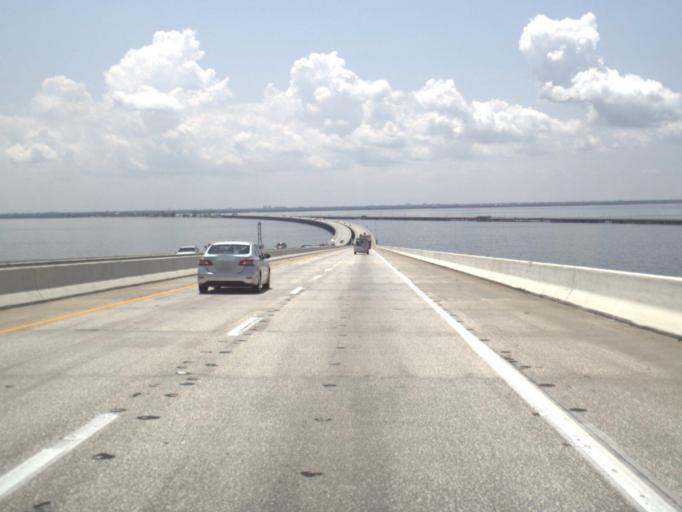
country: US
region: Florida
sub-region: Pinellas County
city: Tierra Verde
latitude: 27.6137
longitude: -82.6508
